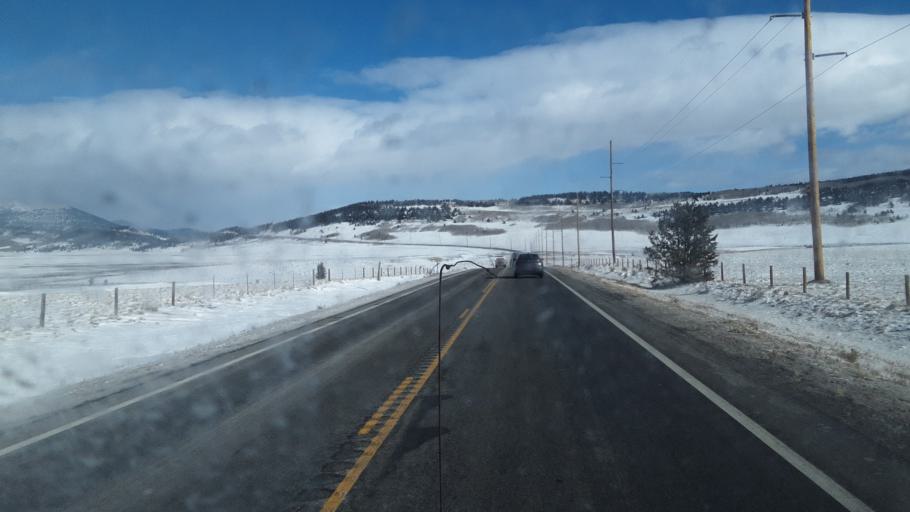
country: US
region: Colorado
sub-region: Park County
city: Fairplay
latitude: 39.2399
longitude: -105.9772
